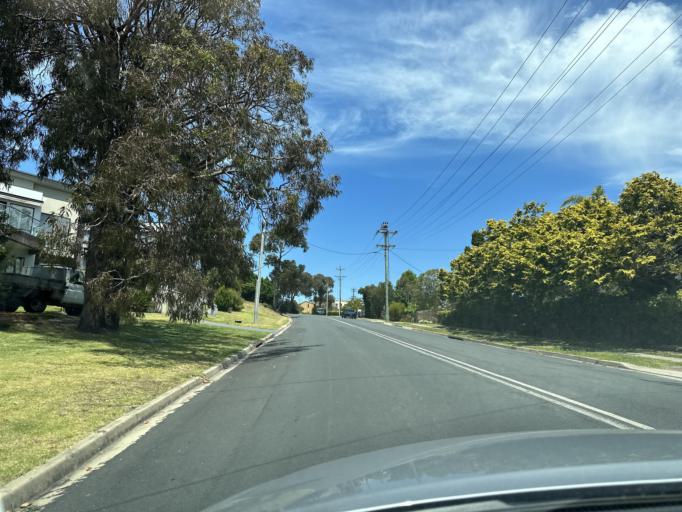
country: AU
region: New South Wales
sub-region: Bega Valley
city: Merimbula
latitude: -36.8906
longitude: 149.9076
